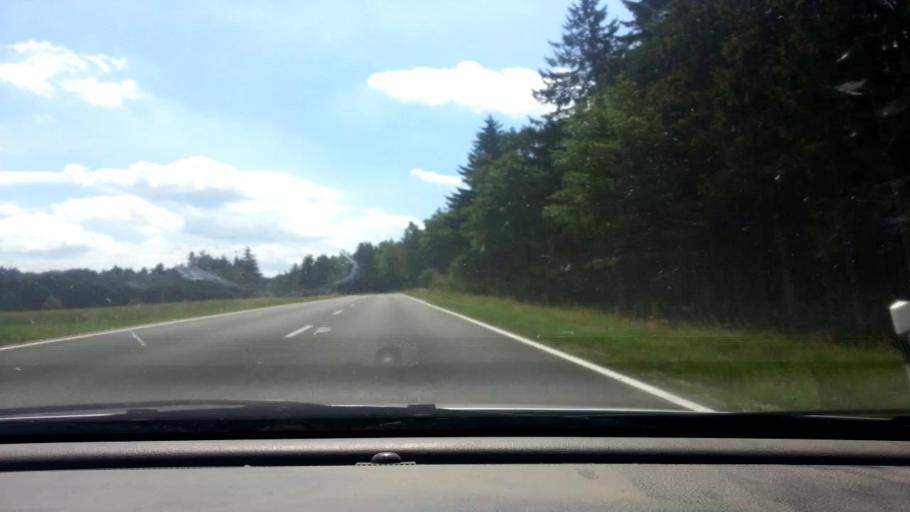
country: DE
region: Bavaria
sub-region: Upper Palatinate
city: Erbendorf
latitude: 49.8471
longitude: 11.9978
